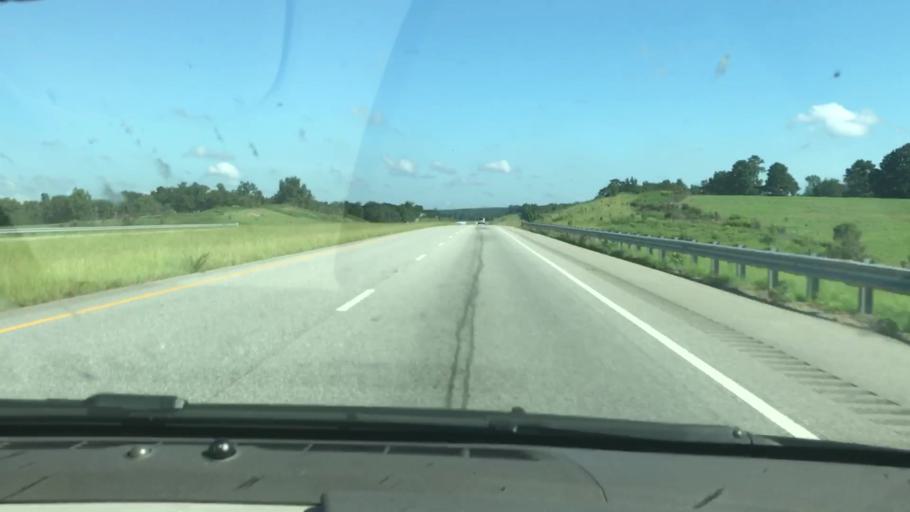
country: US
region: Alabama
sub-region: Barbour County
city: Eufaula
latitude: 32.0950
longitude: -85.1502
